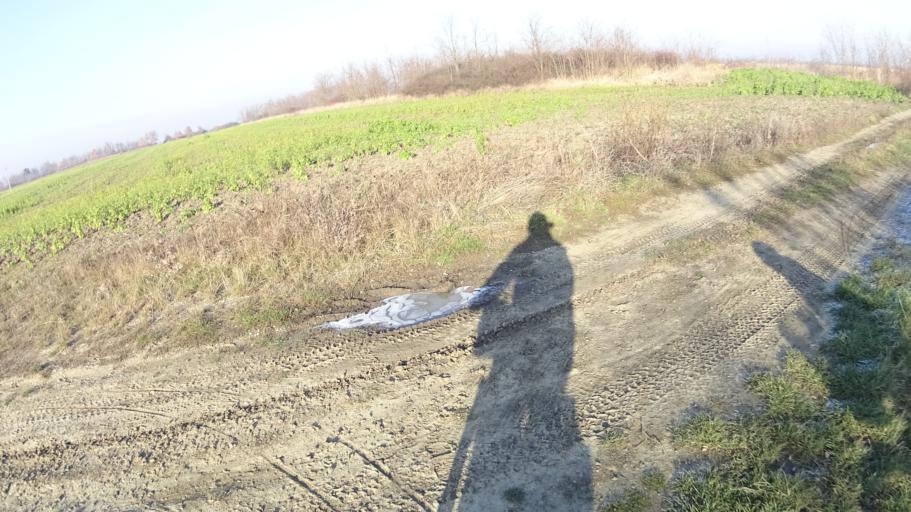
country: HU
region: Borsod-Abauj-Zemplen
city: Nyekladhaza
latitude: 47.9932
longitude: 20.8735
